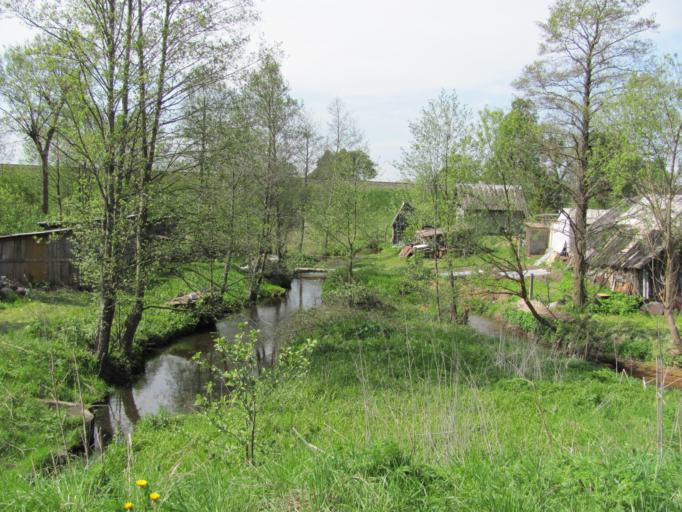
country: LT
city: Nemencine
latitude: 54.7981
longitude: 25.5184
